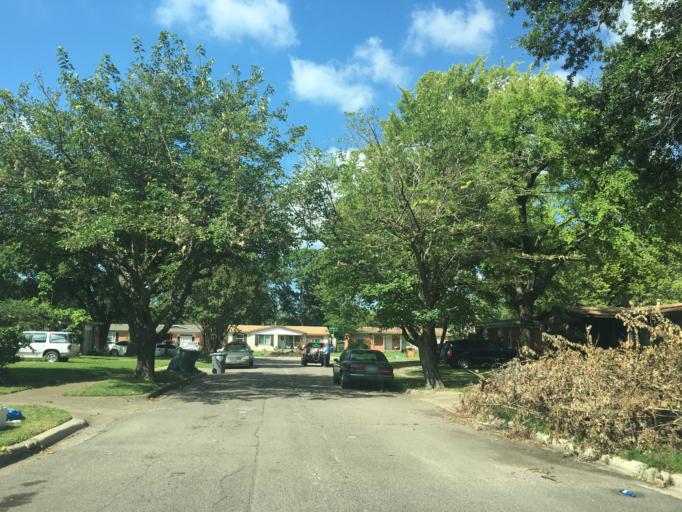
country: US
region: Texas
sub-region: Dallas County
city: Garland
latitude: 32.8406
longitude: -96.6569
